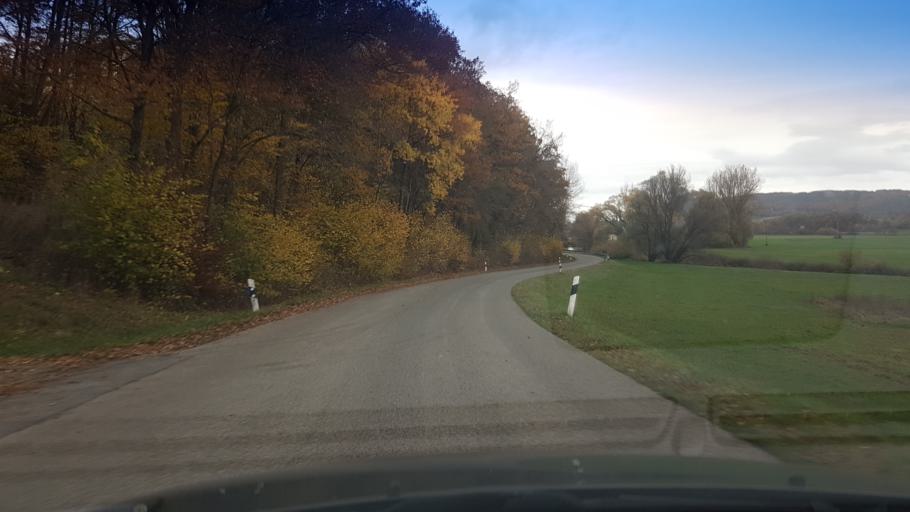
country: DE
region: Bavaria
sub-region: Upper Franconia
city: Rattelsdorf
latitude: 50.0412
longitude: 10.8750
